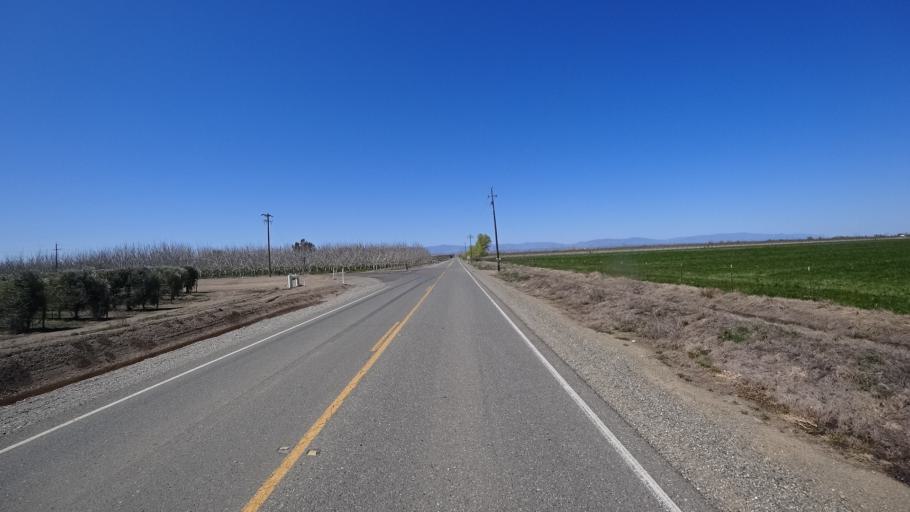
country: US
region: California
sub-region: Glenn County
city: Willows
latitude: 39.6247
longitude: -122.2493
